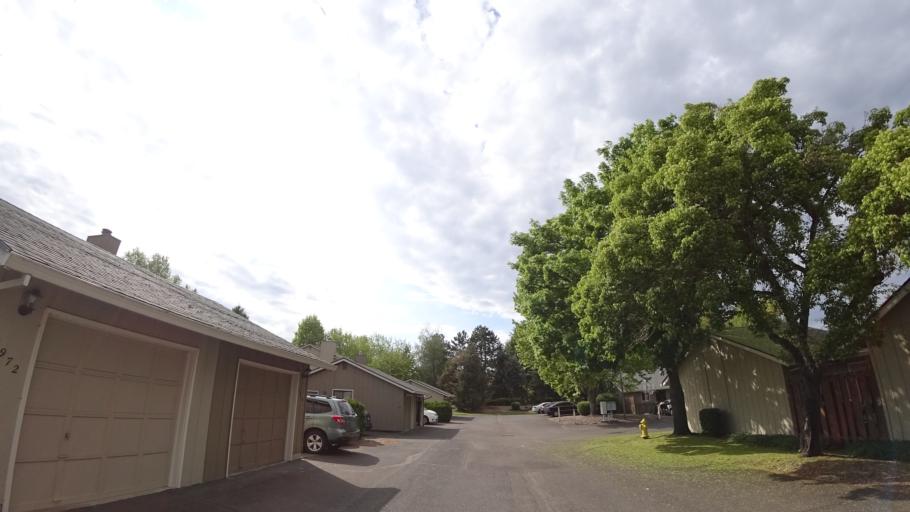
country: US
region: Oregon
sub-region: Washington County
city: Hillsboro
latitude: 45.4972
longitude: -122.9595
